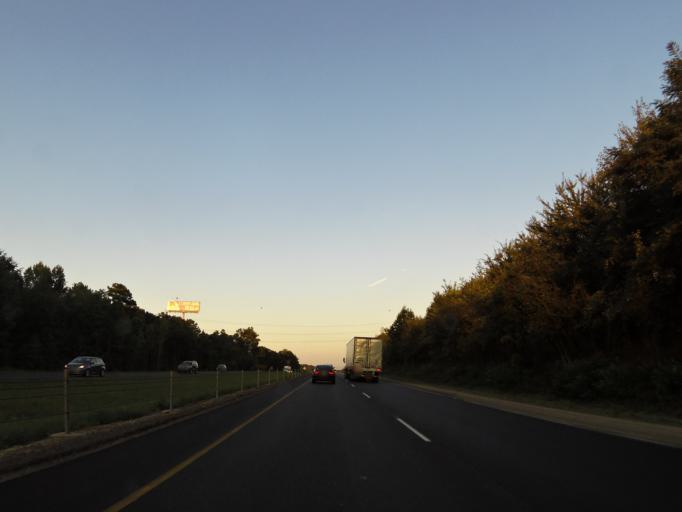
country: US
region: Tennessee
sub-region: Roane County
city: Kingston
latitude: 35.8722
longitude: -84.4823
